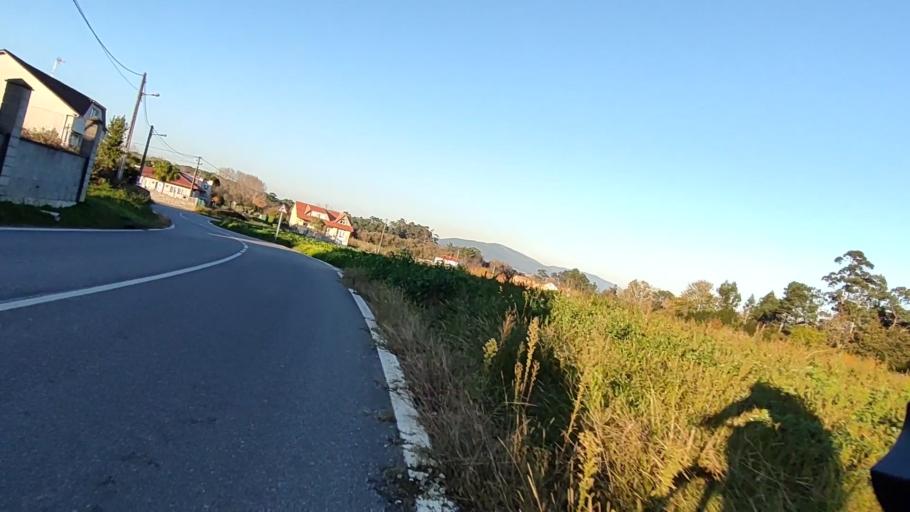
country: ES
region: Galicia
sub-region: Provincia da Coruna
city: Rianxo
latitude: 42.6339
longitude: -8.8579
